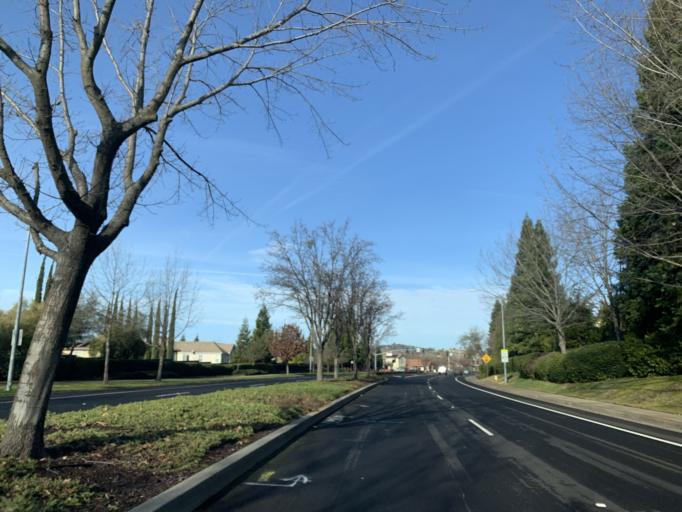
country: US
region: California
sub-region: El Dorado County
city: El Dorado Hills
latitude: 38.6760
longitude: -121.1076
